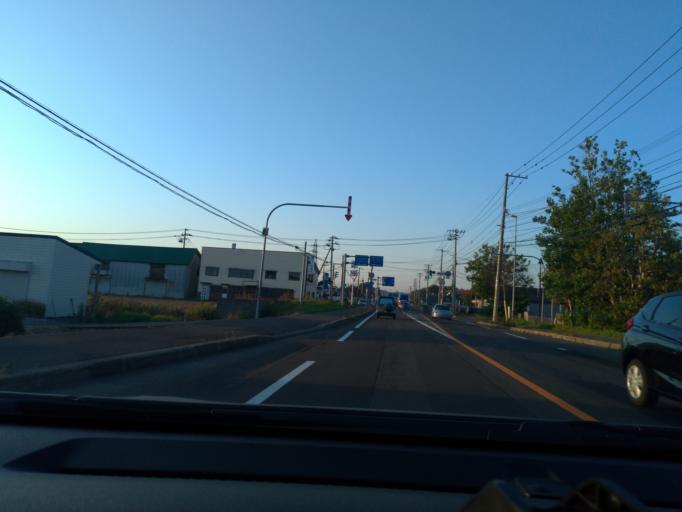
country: JP
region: Hokkaido
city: Tobetsu
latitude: 43.2088
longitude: 141.5191
